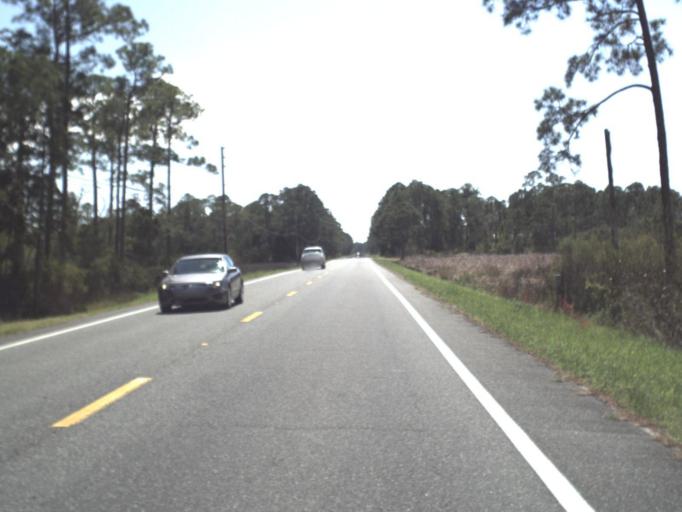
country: US
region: Florida
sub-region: Wakulla County
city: Crawfordville
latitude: 30.0143
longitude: -84.3934
